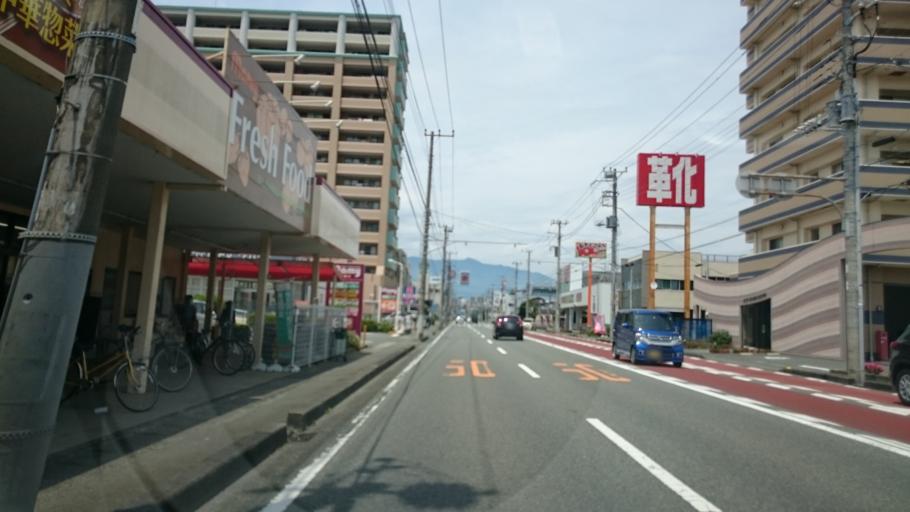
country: JP
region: Shizuoka
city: Numazu
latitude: 35.0896
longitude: 138.8665
